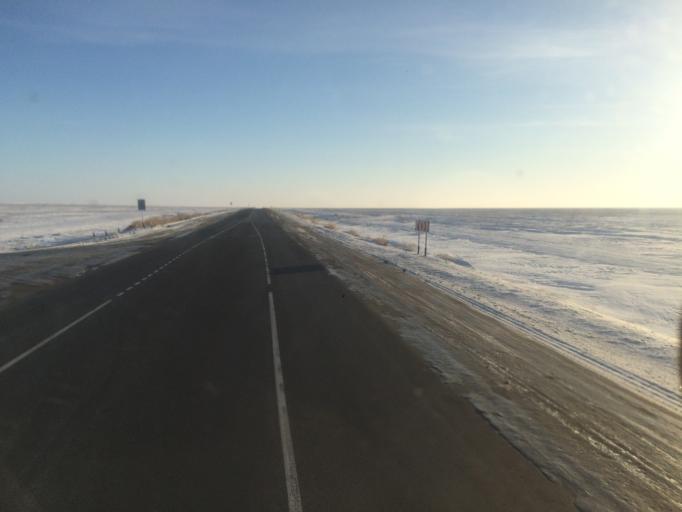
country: KZ
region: Aqtoebe
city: Yrghyz
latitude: 48.3886
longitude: 61.1129
